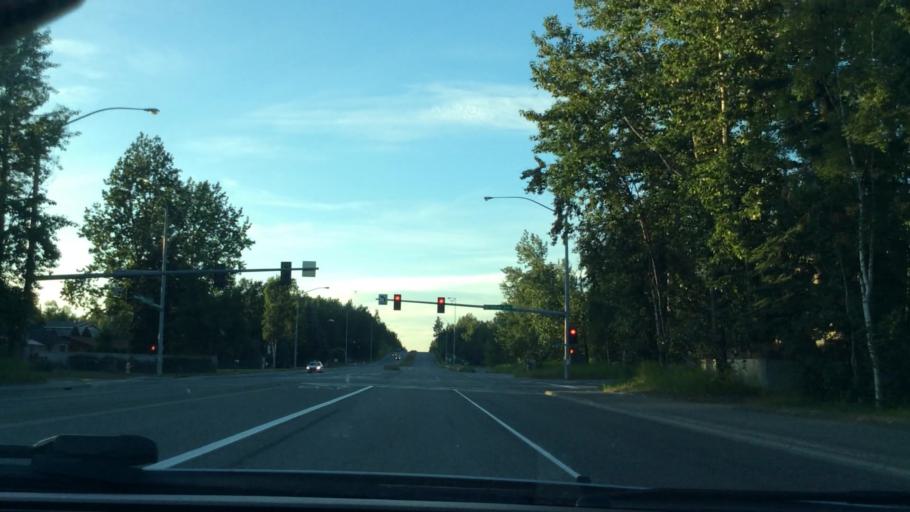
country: US
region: Alaska
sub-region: Anchorage Municipality
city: Anchorage
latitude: 61.1983
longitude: -149.7783
